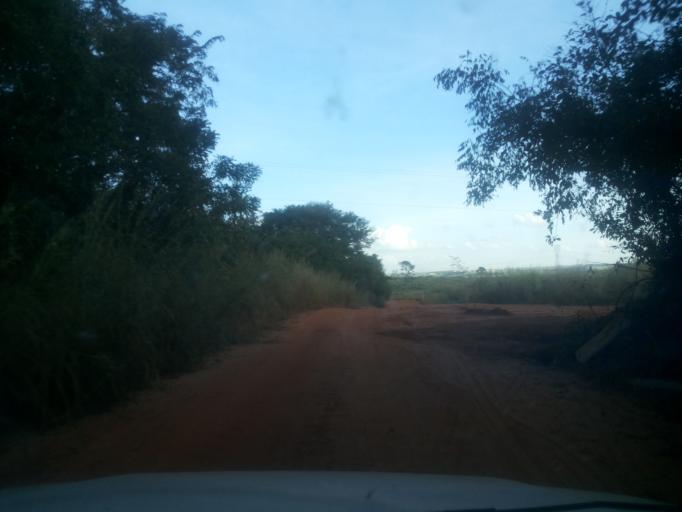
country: BR
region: Minas Gerais
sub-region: Santa Vitoria
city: Santa Vitoria
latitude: -19.0087
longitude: -50.3723
